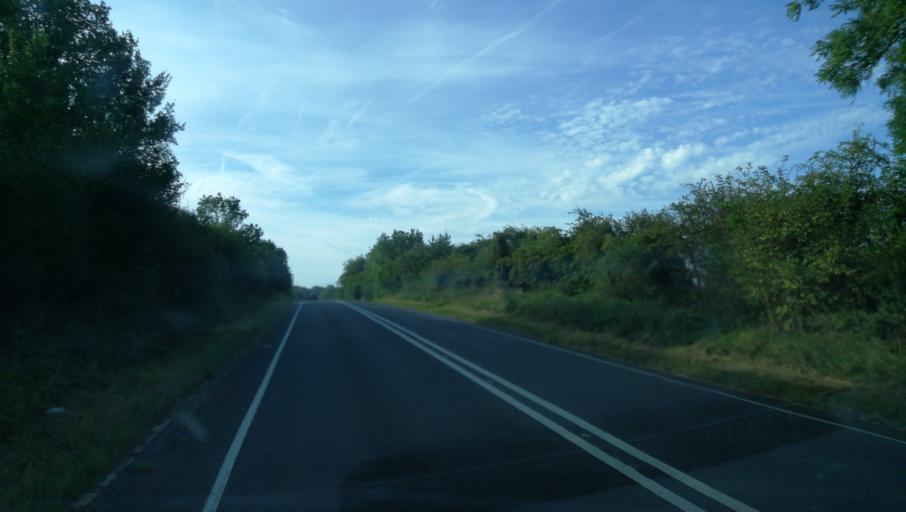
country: GB
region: England
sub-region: Oxfordshire
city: Deddington
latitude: 51.9623
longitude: -1.3199
